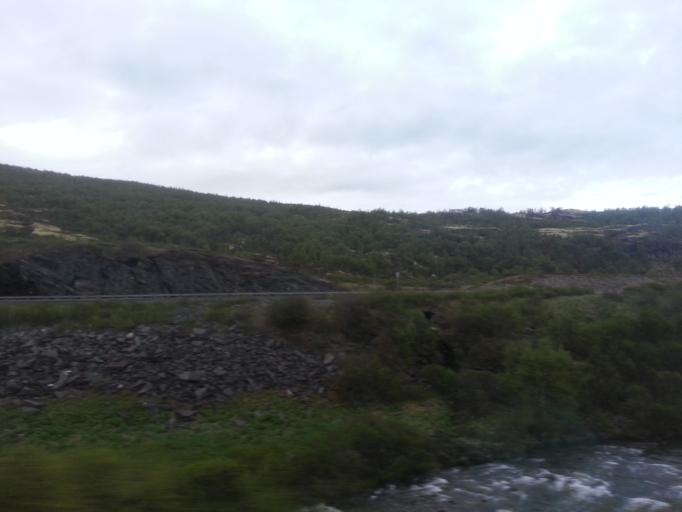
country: NO
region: Sor-Trondelag
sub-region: Oppdal
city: Oppdal
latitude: 62.3007
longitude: 9.5997
